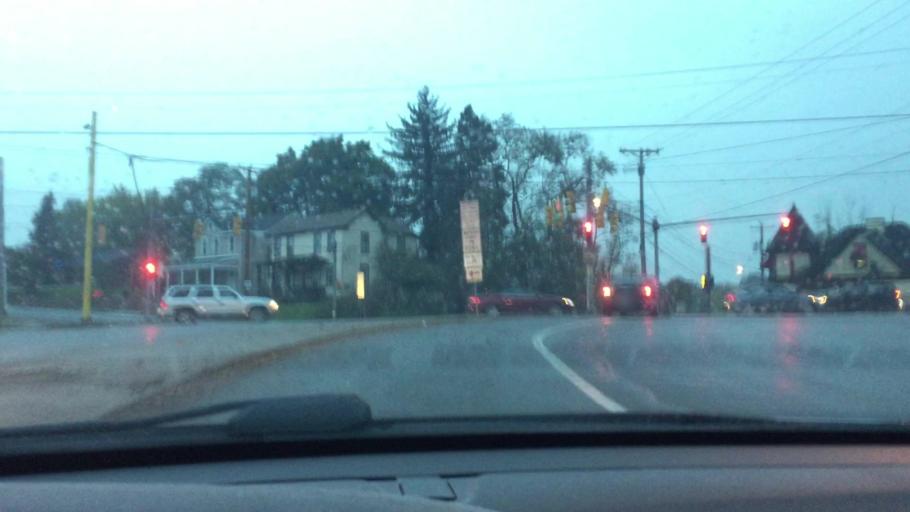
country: US
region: Pennsylvania
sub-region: Allegheny County
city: Ingram
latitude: 40.4409
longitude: -80.0806
